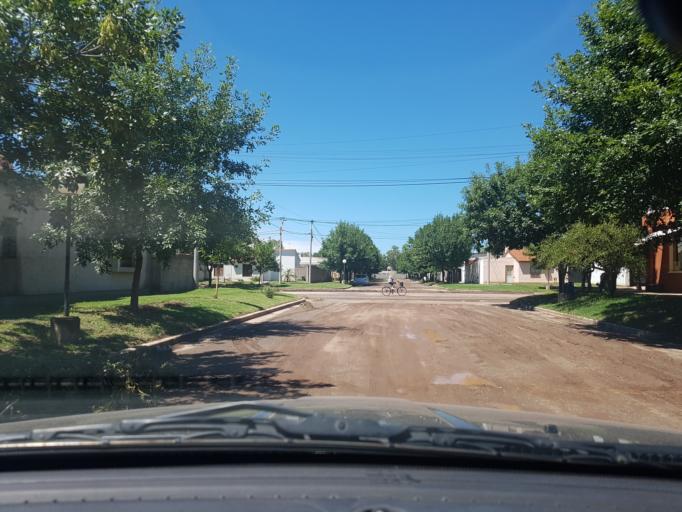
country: AR
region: Cordoba
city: Las Perdices
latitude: -32.7592
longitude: -63.7745
